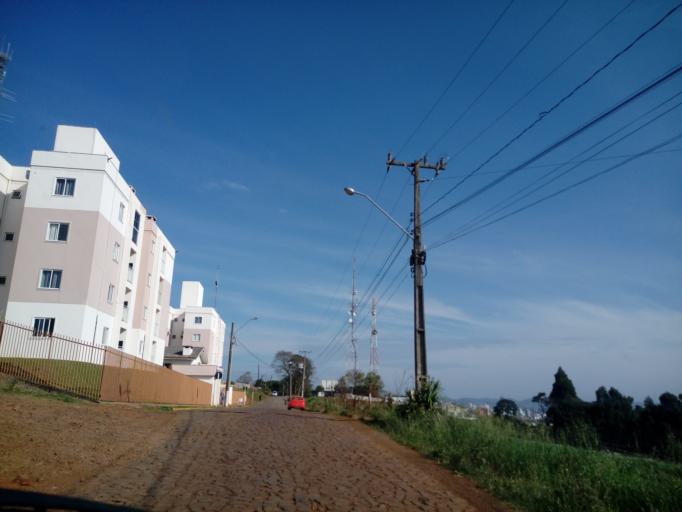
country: BR
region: Santa Catarina
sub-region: Chapeco
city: Chapeco
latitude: -27.1067
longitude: -52.5790
